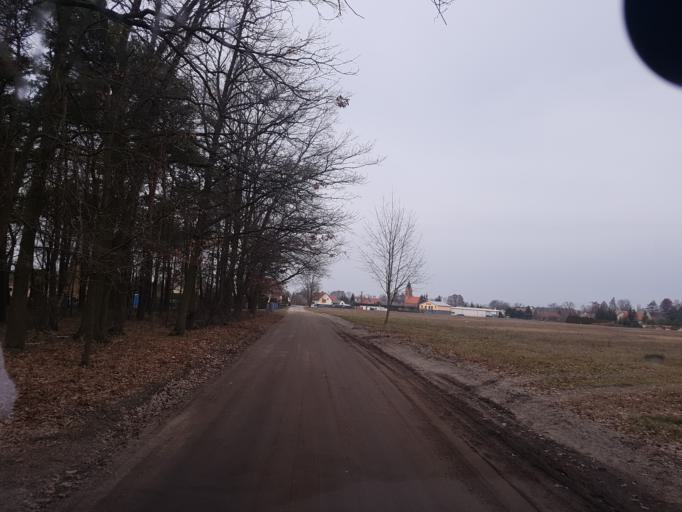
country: DE
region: Brandenburg
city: Sonnewalde
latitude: 51.6646
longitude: 13.6496
